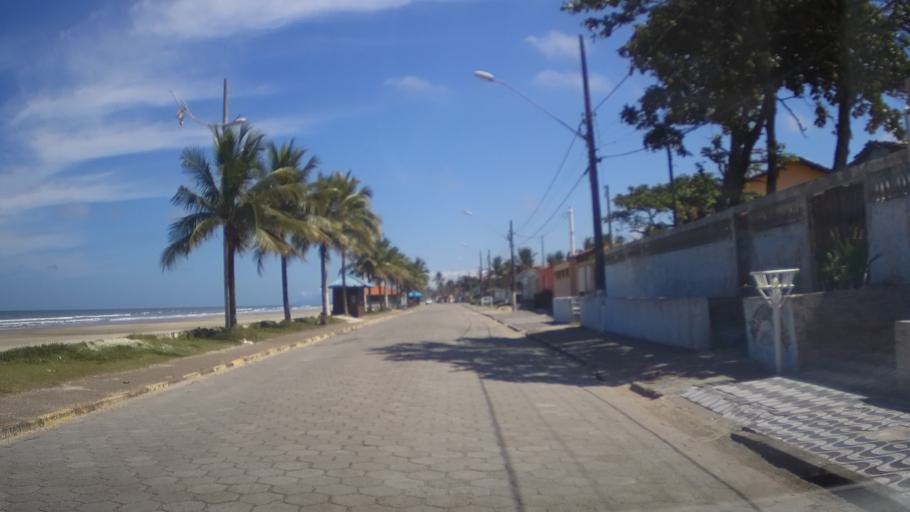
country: BR
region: Sao Paulo
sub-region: Mongagua
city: Mongagua
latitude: -24.1375
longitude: -46.7004
